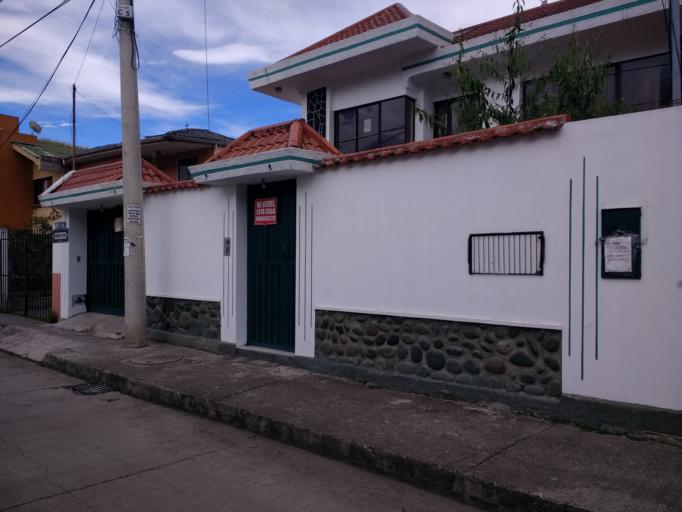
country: EC
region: Azuay
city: Cuenca
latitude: -2.9017
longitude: -79.0324
